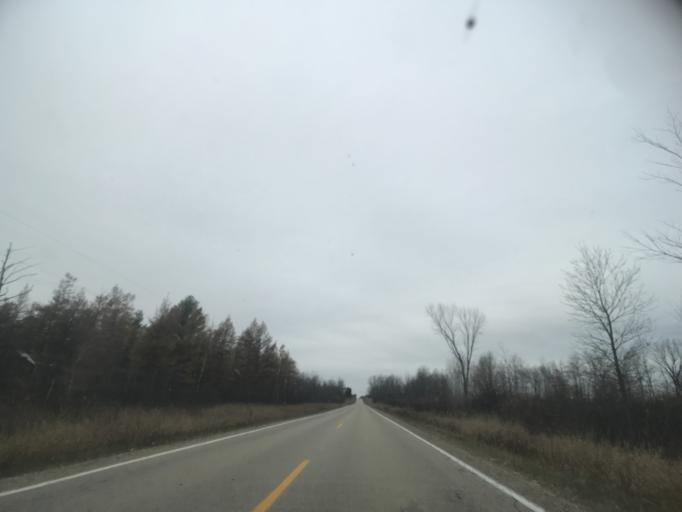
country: US
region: Wisconsin
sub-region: Oconto County
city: Gillett
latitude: 44.9835
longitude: -88.3038
